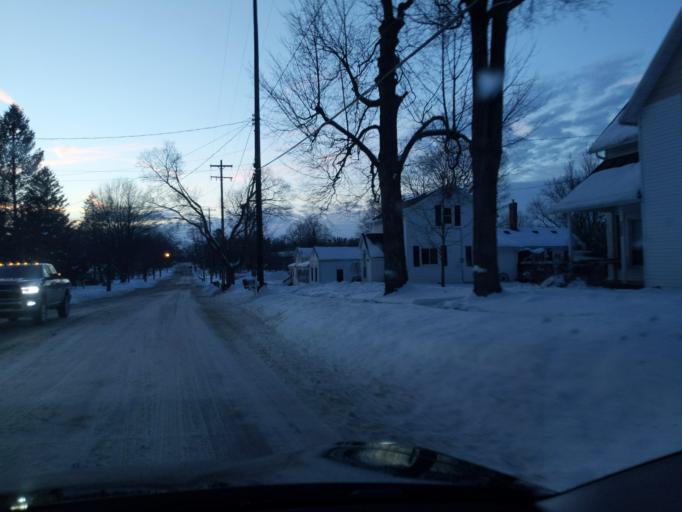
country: US
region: Michigan
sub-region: Ingham County
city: Mason
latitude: 42.5822
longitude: -84.4386
